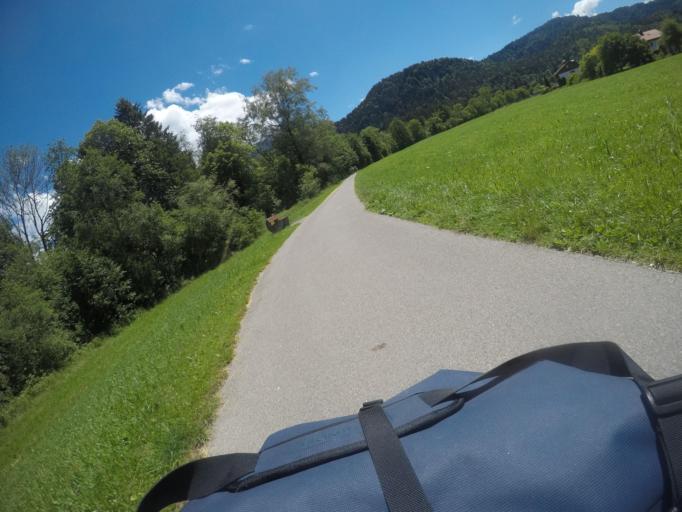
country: DE
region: Bavaria
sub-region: Swabia
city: Fuessen
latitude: 47.5711
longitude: 10.7116
